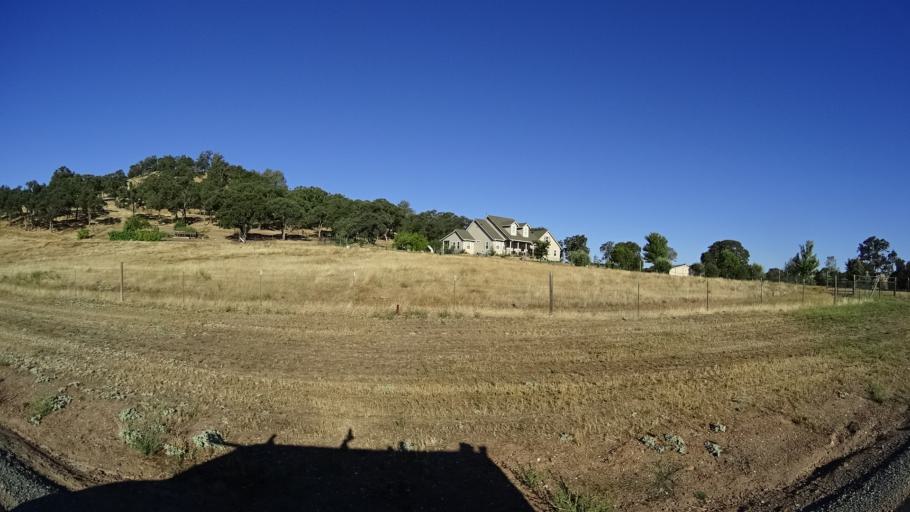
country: US
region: California
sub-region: Calaveras County
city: Valley Springs
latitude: 38.2308
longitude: -120.7629
